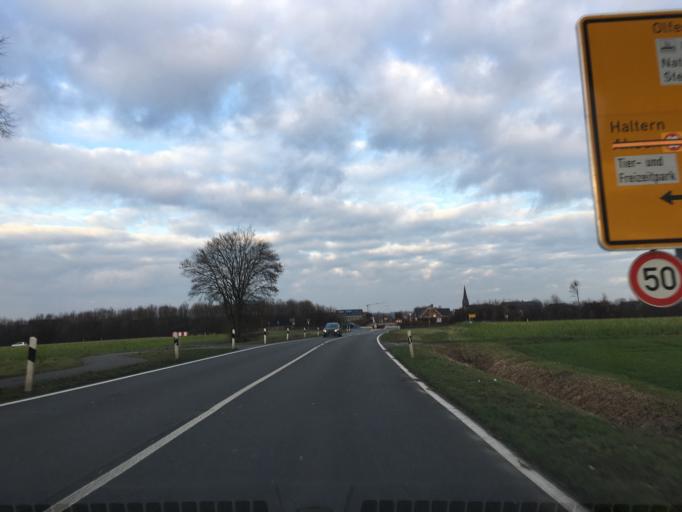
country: DE
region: North Rhine-Westphalia
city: Olfen
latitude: 51.6996
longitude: 7.3685
